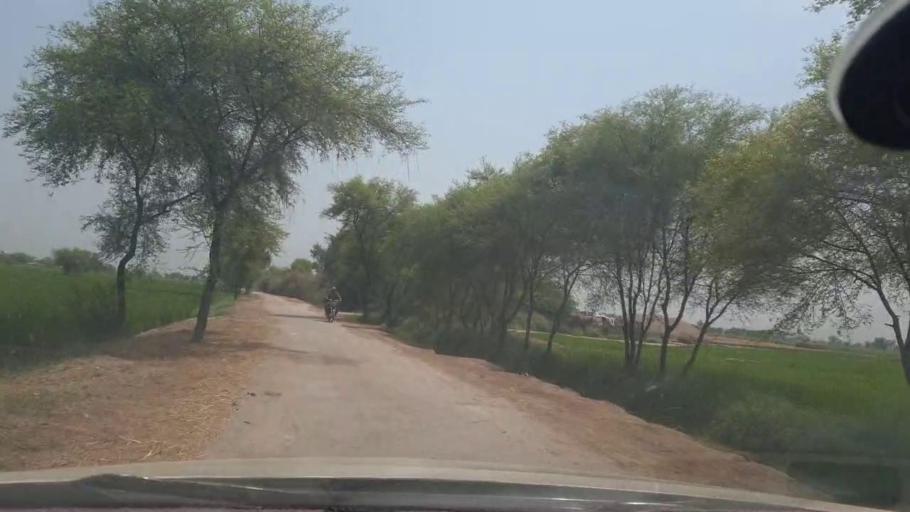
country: PK
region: Sindh
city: Jacobabad
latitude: 28.1780
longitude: 68.3824
